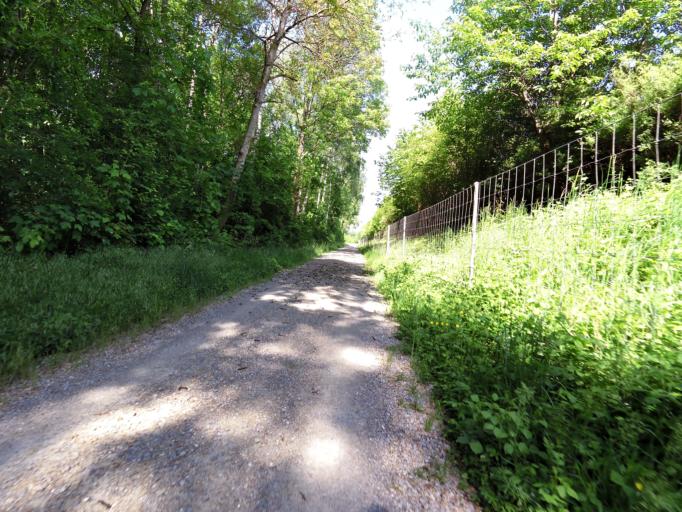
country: CH
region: Thurgau
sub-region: Frauenfeld District
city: Frauenfeld
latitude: 47.5791
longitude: 8.9240
